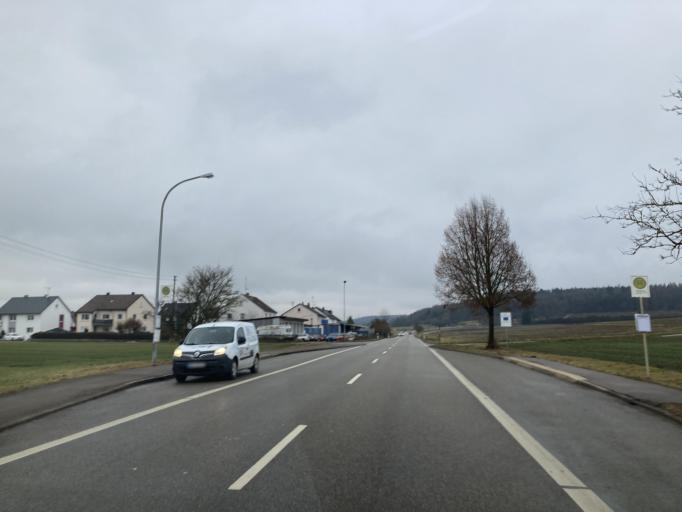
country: DE
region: Baden-Wuerttemberg
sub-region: Regierungsbezirk Stuttgart
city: Sontheim an der Brenz
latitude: 48.5673
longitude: 10.2940
